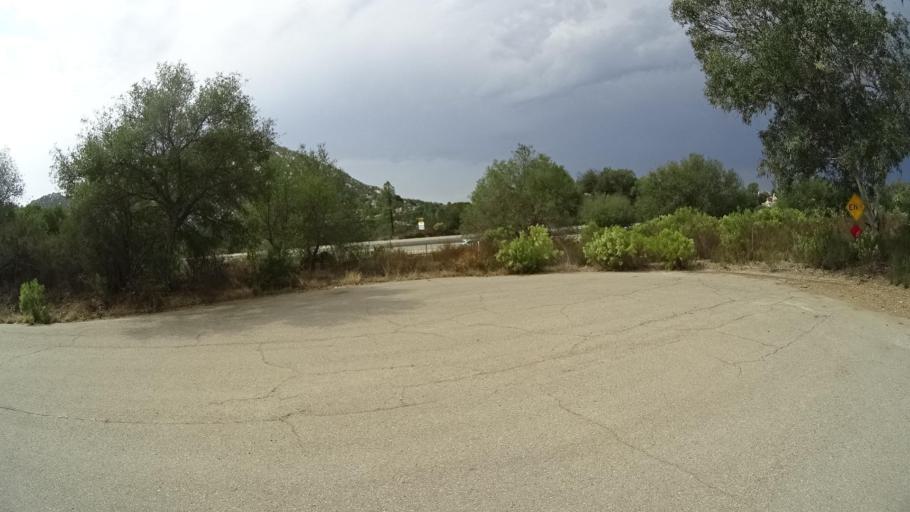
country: US
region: California
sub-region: San Diego County
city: San Pasqual
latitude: 33.0104
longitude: -116.9538
